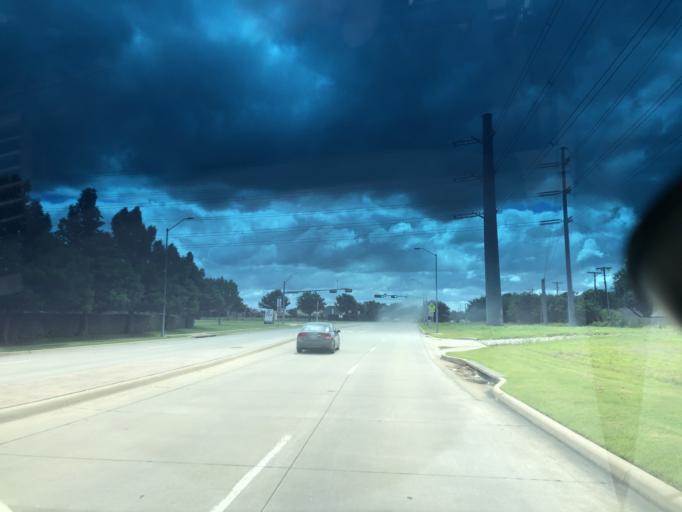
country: US
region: Texas
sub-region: Dallas County
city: Grand Prairie
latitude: 32.6985
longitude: -97.0235
